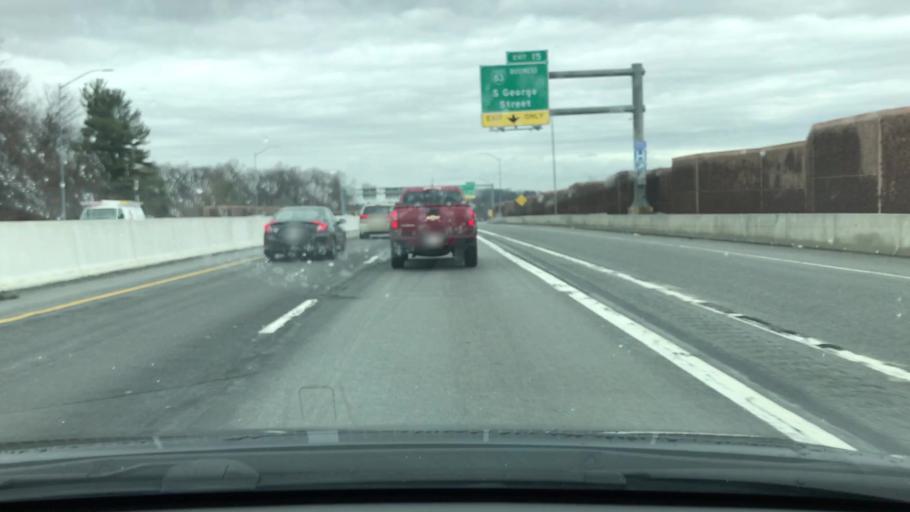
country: US
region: Pennsylvania
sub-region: York County
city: Spry
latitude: 39.9133
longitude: -76.7038
